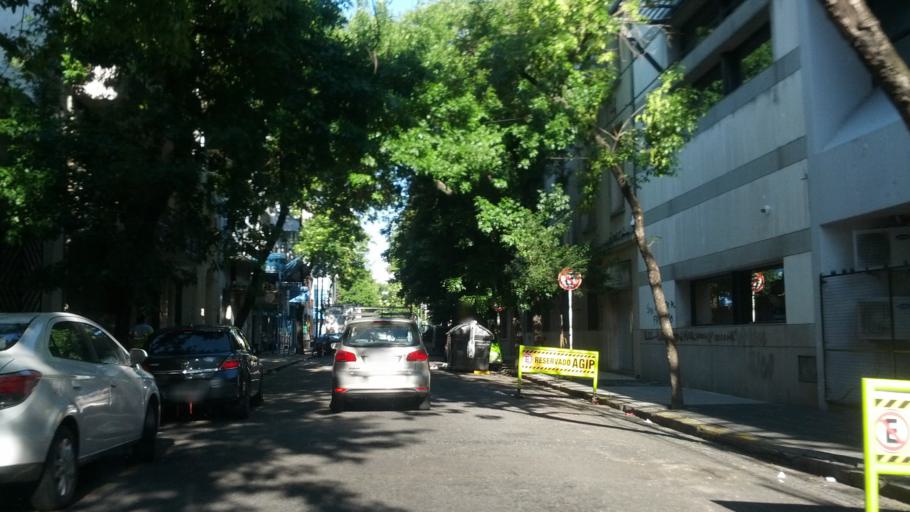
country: AR
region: Buenos Aires F.D.
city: Buenos Aires
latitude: -34.6240
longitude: -58.3896
